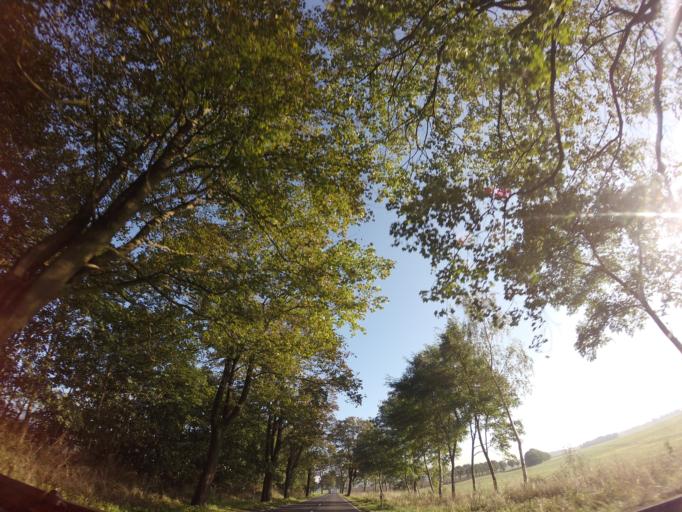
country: PL
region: West Pomeranian Voivodeship
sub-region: Powiat stargardzki
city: Stargard Szczecinski
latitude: 53.3650
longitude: 15.0676
